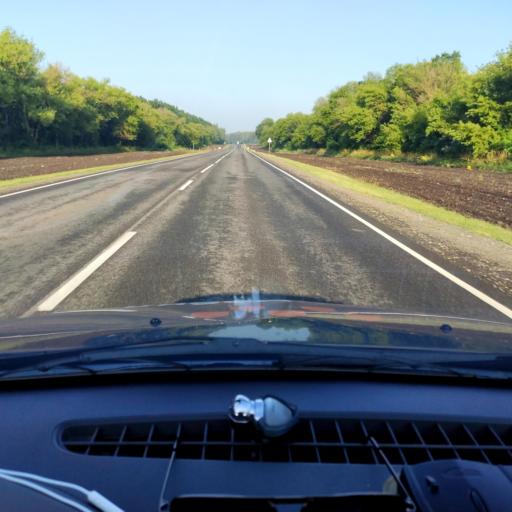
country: RU
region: Orjol
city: Livny
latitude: 52.4343
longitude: 37.8701
